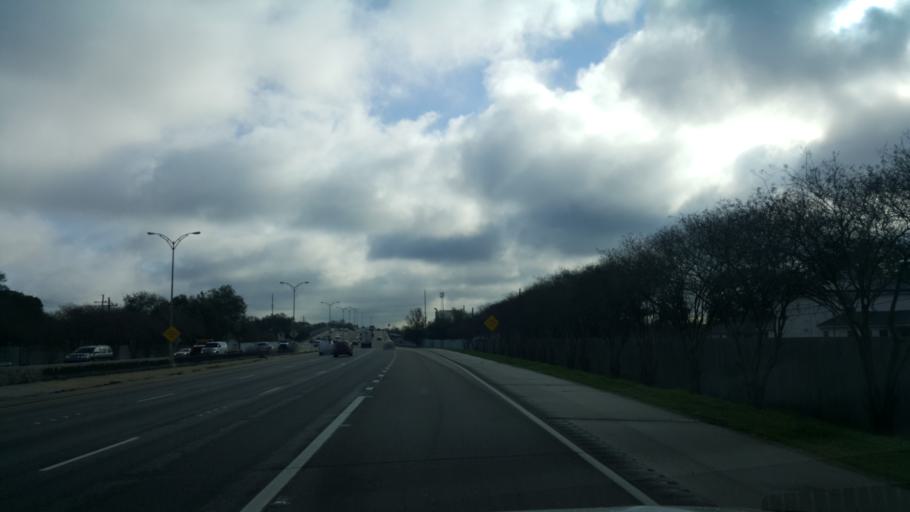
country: US
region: Louisiana
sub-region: Jefferson Parish
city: Metairie
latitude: 29.9955
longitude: -90.1062
